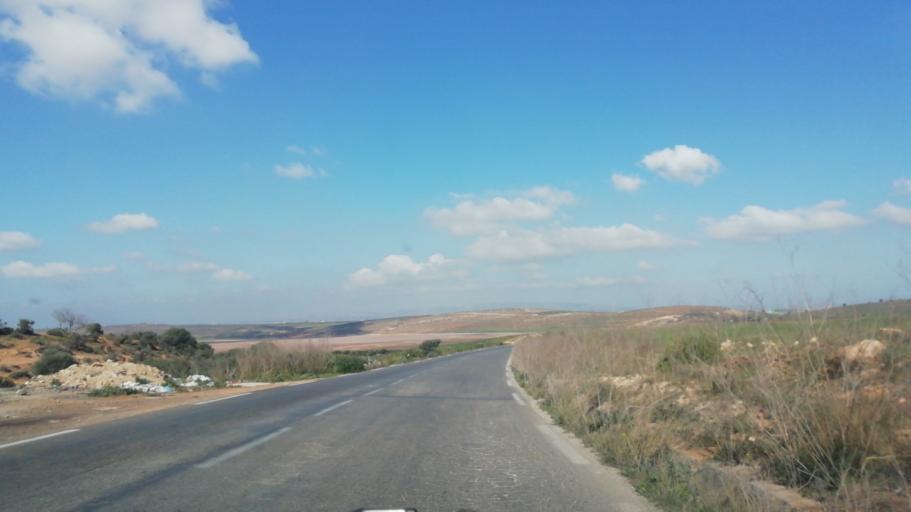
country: DZ
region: Oran
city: Ain el Bya
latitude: 35.7290
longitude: -0.2508
